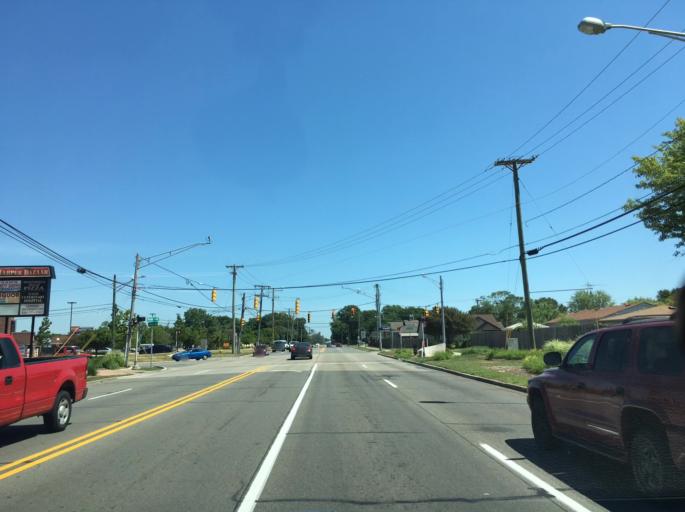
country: US
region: Michigan
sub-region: Macomb County
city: Saint Clair Shores
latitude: 42.5396
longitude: -82.8824
